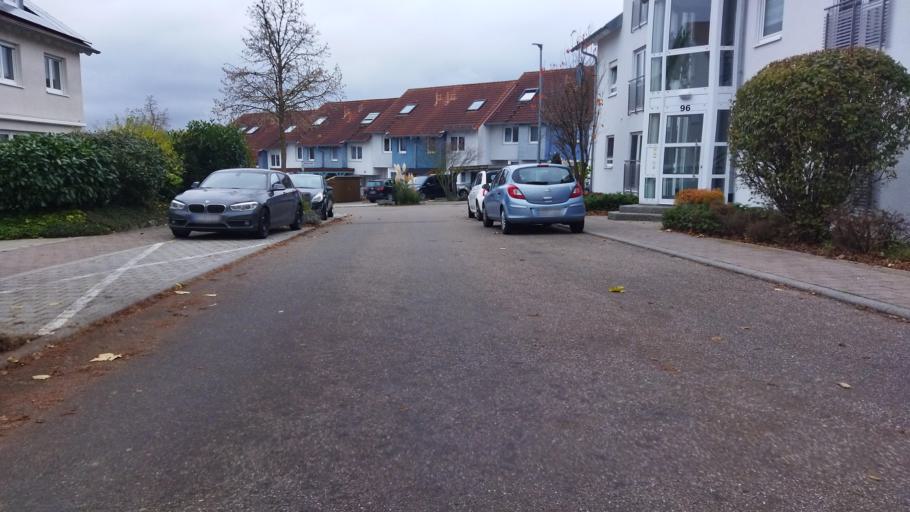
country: DE
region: Baden-Wuerttemberg
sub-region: Regierungsbezirk Stuttgart
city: Leingarten
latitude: 49.1412
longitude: 9.1055
